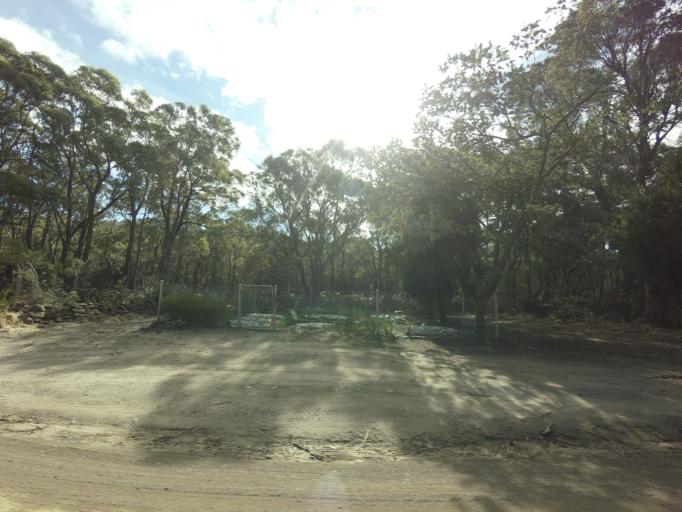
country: AU
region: Tasmania
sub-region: Clarence
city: Sandford
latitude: -43.0839
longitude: 147.6839
